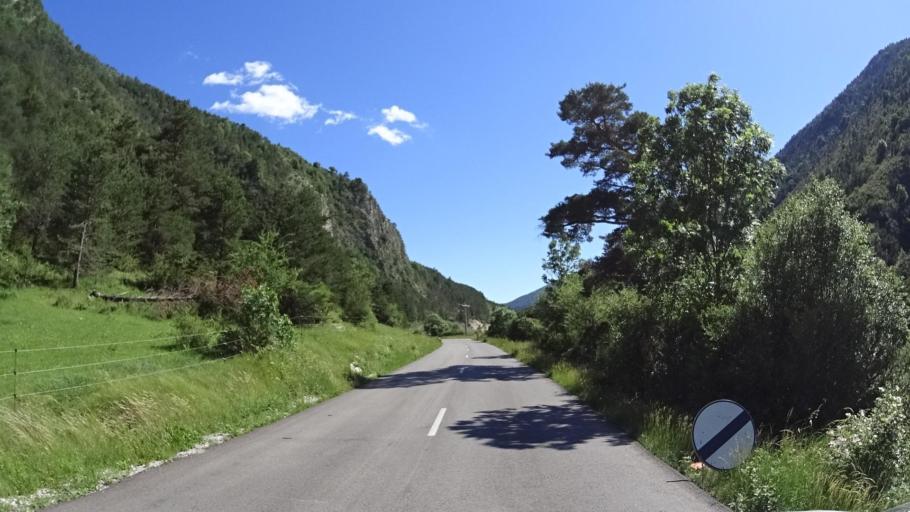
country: FR
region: Provence-Alpes-Cote d'Azur
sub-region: Departement des Alpes-de-Haute-Provence
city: Annot
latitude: 44.0561
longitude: 6.5735
